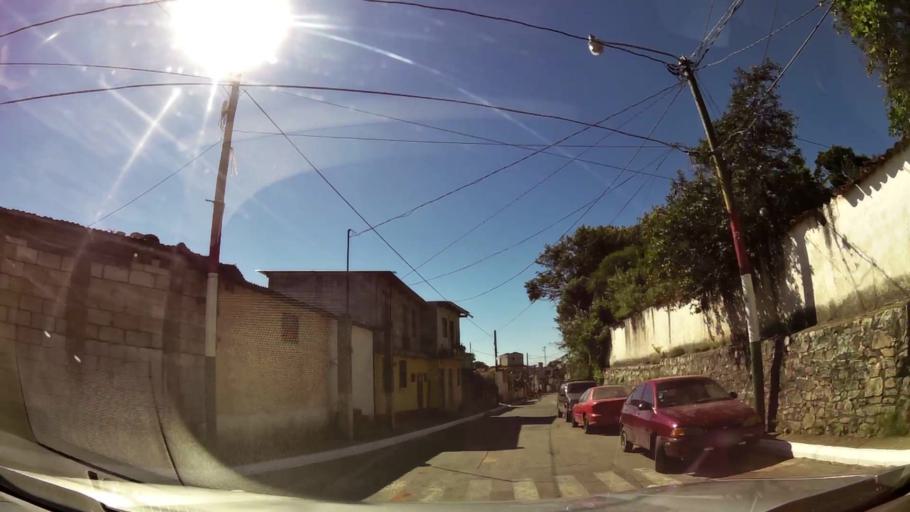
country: GT
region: Guatemala
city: Fraijanes
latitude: 14.4619
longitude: -90.4402
